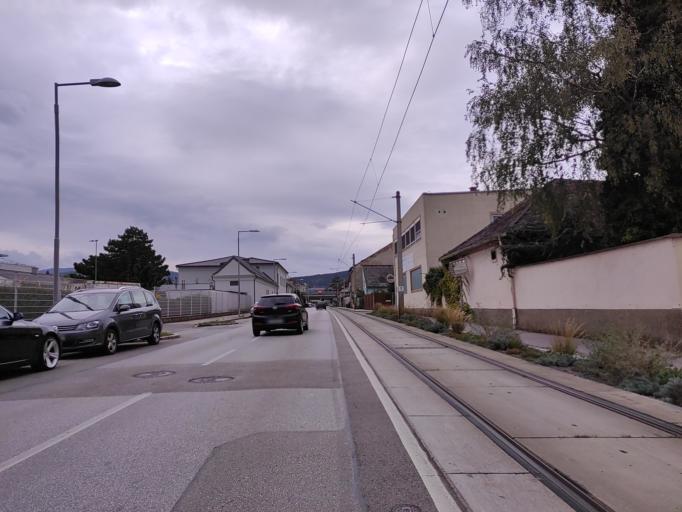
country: AT
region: Lower Austria
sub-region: Politischer Bezirk Baden
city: Baden
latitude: 48.0022
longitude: 16.2451
